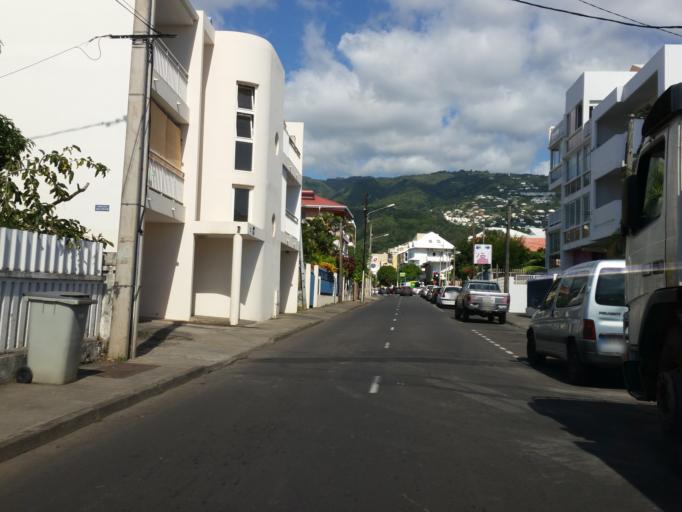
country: RE
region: Reunion
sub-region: Reunion
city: Saint-Denis
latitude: -20.8858
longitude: 55.4591
